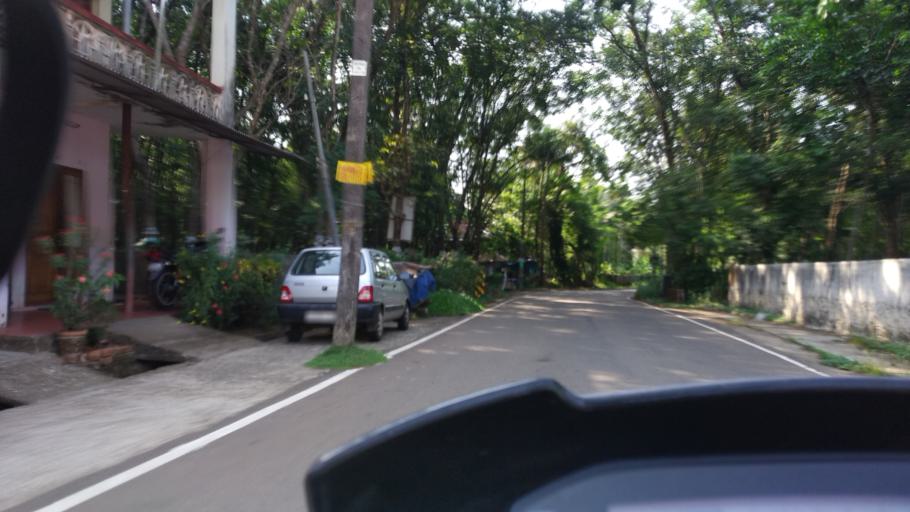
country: IN
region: Kerala
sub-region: Ernakulam
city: Piravam
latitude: 9.8522
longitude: 76.5313
